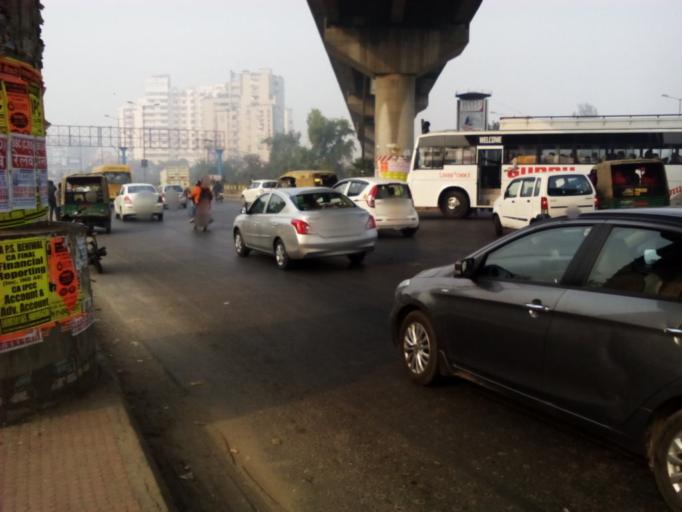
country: IN
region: Uttar Pradesh
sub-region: Gautam Buddha Nagar
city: Noida
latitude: 28.6457
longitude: 77.3317
